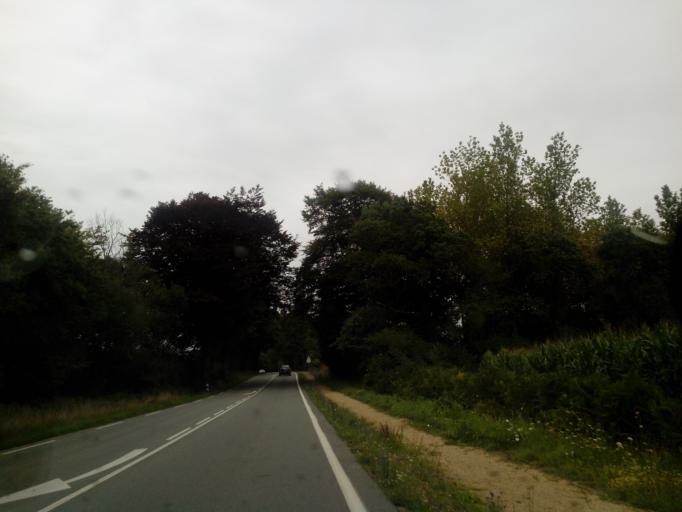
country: FR
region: Brittany
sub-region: Departement du Finistere
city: Quimperle
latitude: 47.8642
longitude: -3.5246
